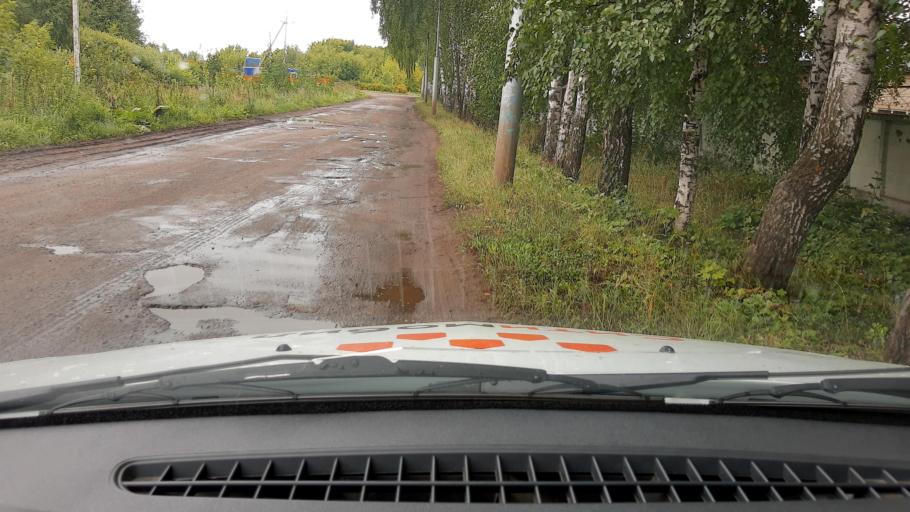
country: RU
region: Bashkortostan
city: Avdon
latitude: 54.7202
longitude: 55.8114
